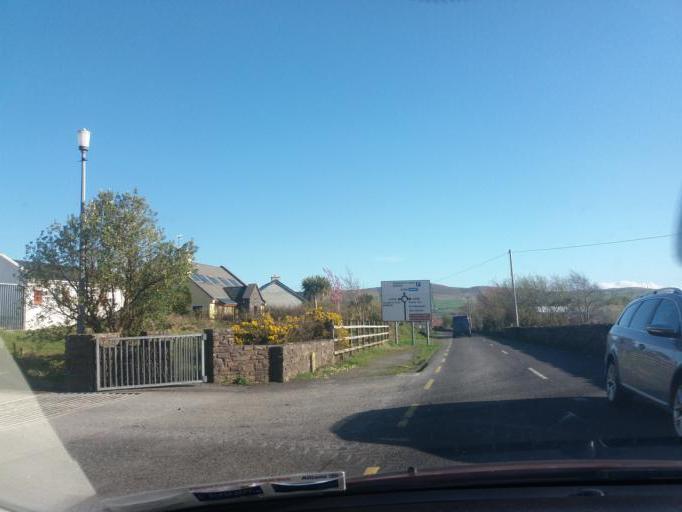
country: IE
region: Munster
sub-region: Ciarrai
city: Dingle
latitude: 52.1453
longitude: -10.2889
